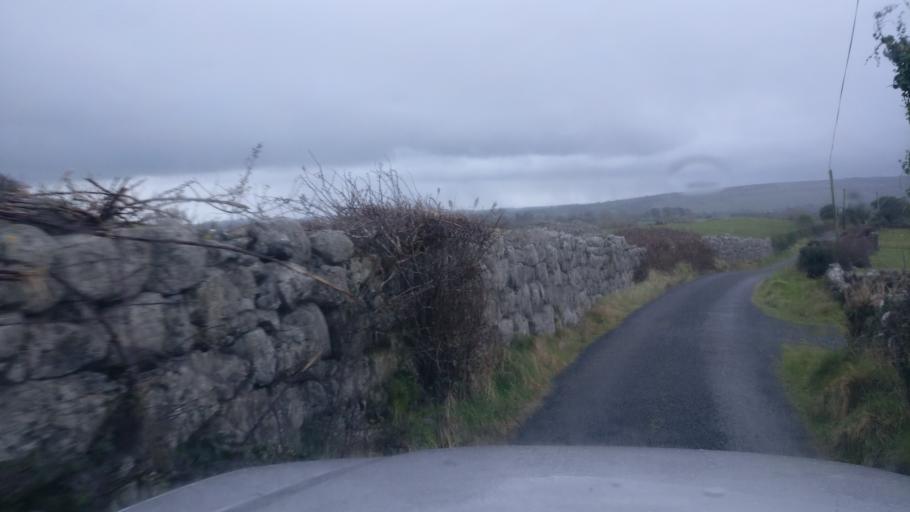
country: IE
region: Connaught
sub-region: County Galway
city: Loughrea
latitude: 53.1940
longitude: -8.6812
